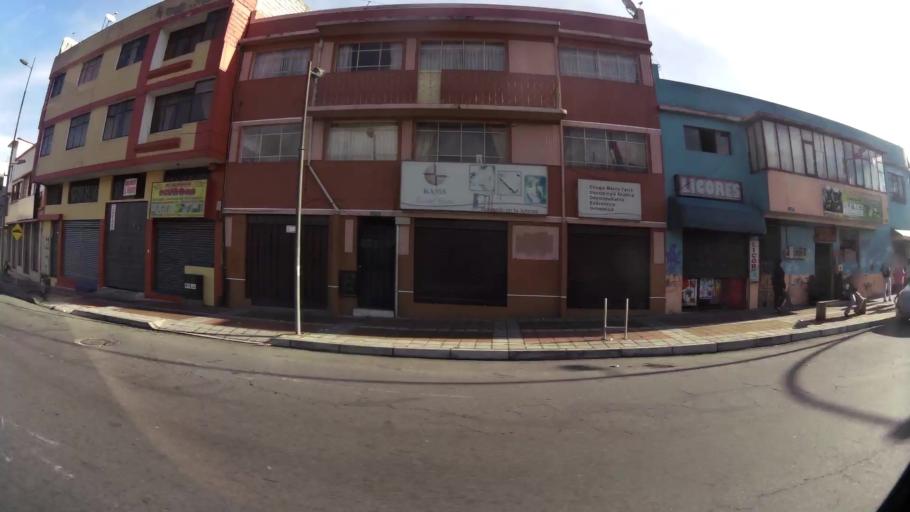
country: EC
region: Pichincha
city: Quito
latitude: -0.2454
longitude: -78.5158
